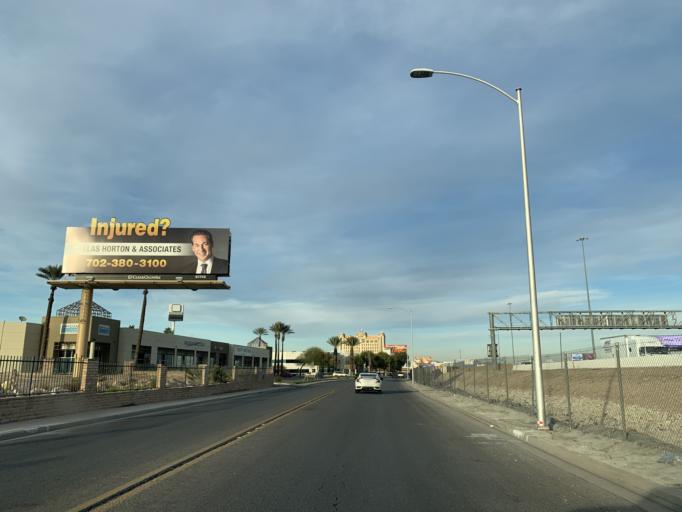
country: US
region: Nevada
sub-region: Clark County
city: Paradise
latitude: 36.1346
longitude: -115.1797
